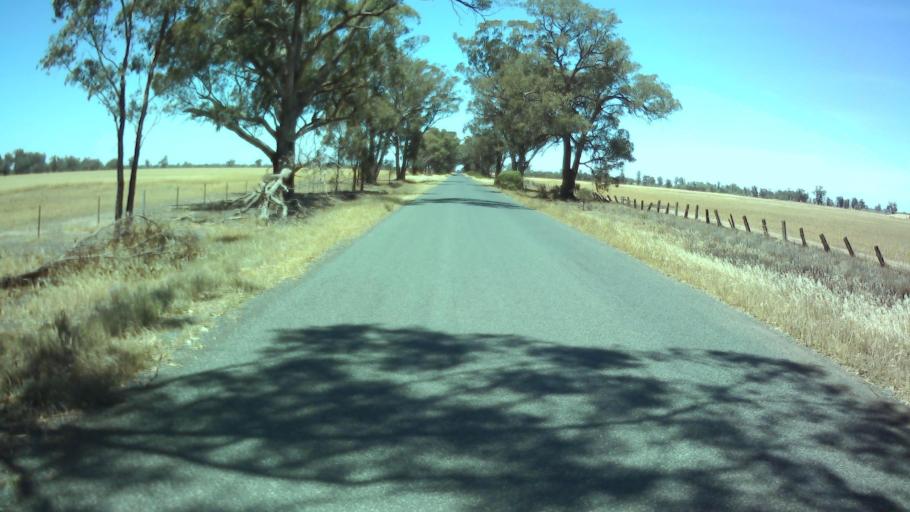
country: AU
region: New South Wales
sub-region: Weddin
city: Grenfell
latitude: -34.0191
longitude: 147.7930
